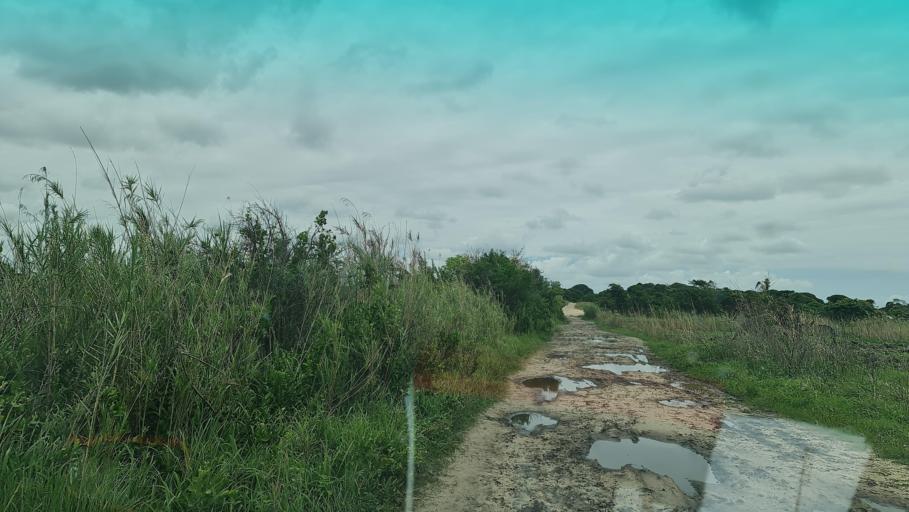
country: MZ
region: Maputo City
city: Maputo
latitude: -25.6996
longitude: 32.7052
